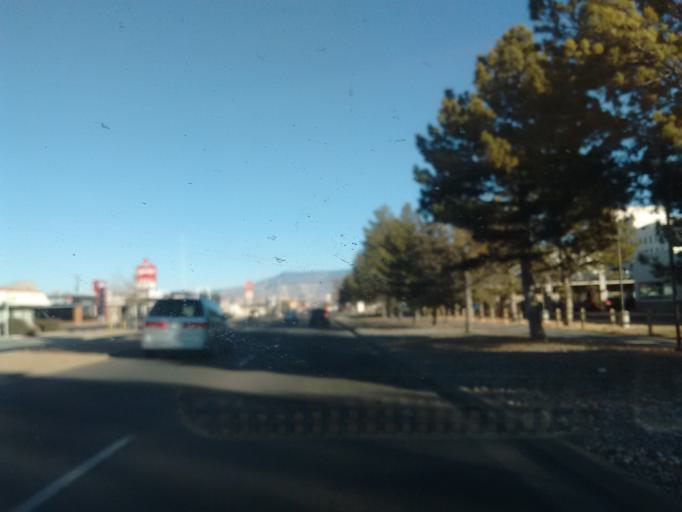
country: US
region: Colorado
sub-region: Mesa County
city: Grand Junction
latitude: 39.0773
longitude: -108.5425
